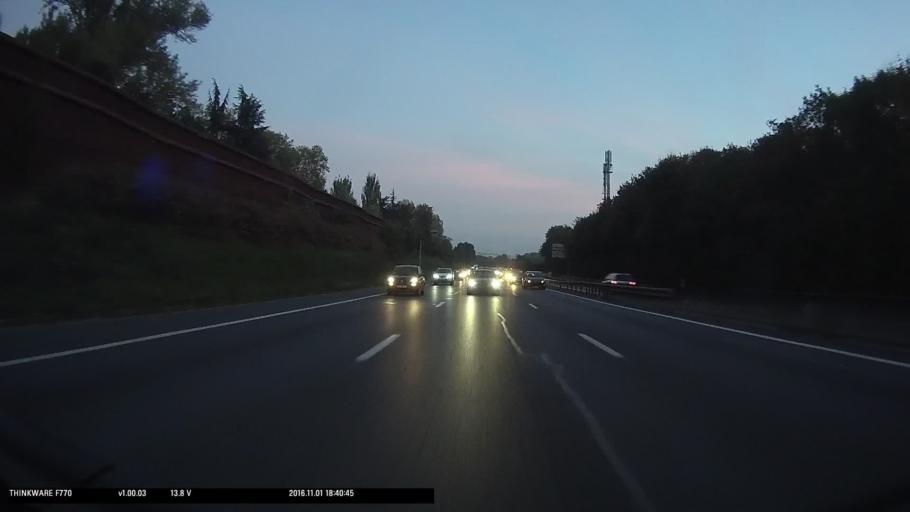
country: FR
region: Ile-de-France
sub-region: Departement de l'Essonne
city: Epinay-sur-Orge
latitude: 48.6856
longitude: 2.3273
